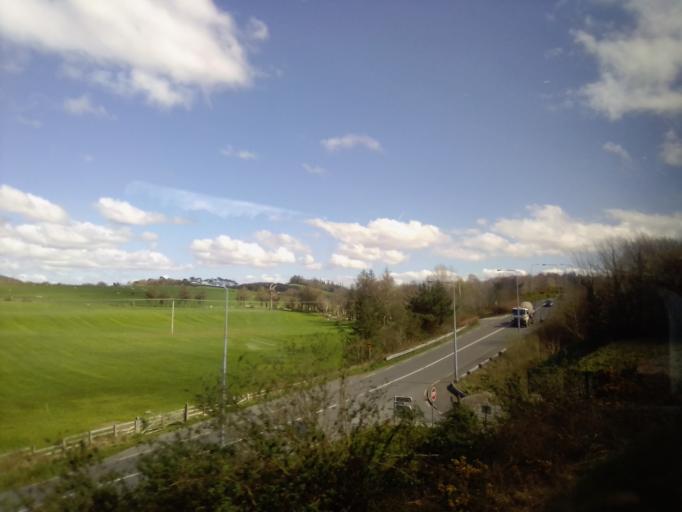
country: IE
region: Munster
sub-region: Ciarrai
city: Cill Airne
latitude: 52.0709
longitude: -9.5065
